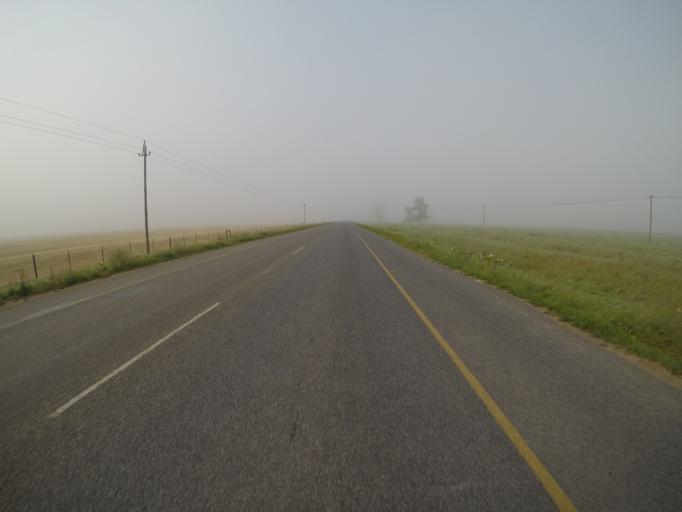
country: ZA
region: Western Cape
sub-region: City of Cape Town
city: Kraaifontein
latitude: -33.6707
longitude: 18.7072
